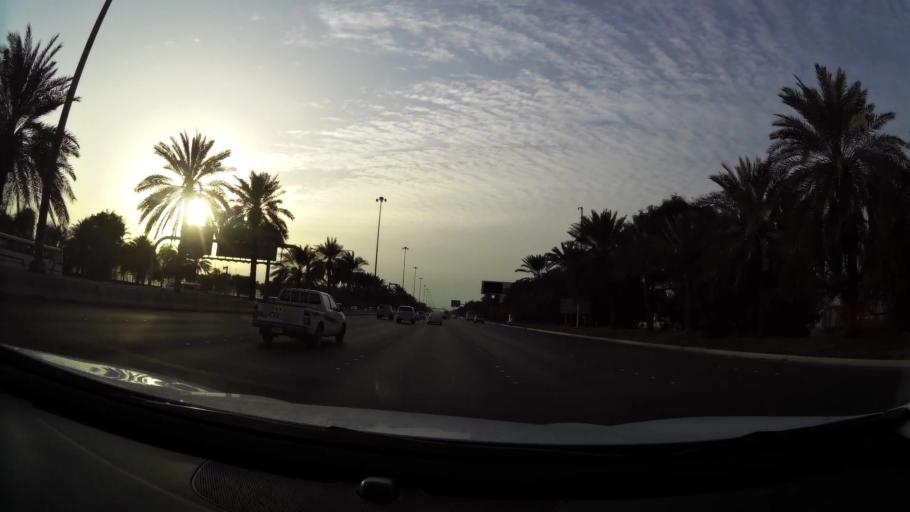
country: AE
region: Abu Dhabi
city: Abu Dhabi
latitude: 24.3970
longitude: 54.5098
